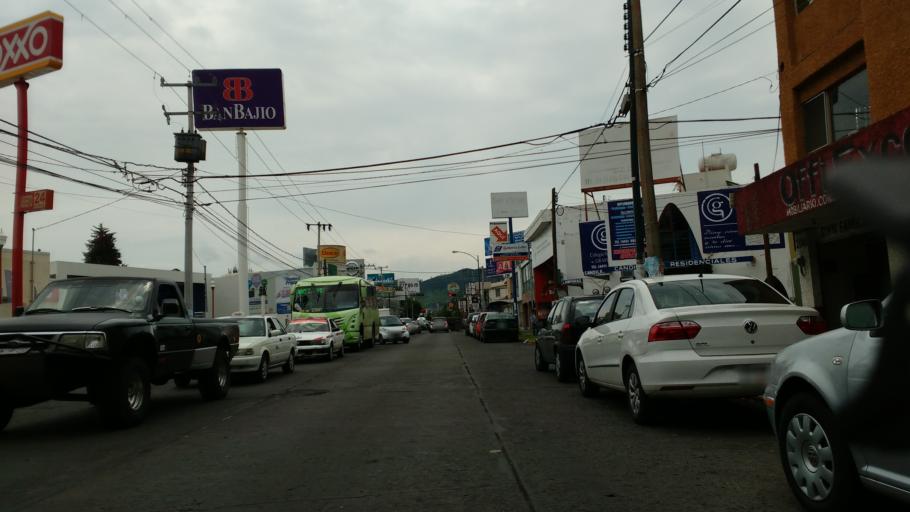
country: MX
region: Michoacan
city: Morelia
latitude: 19.6933
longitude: -101.1752
